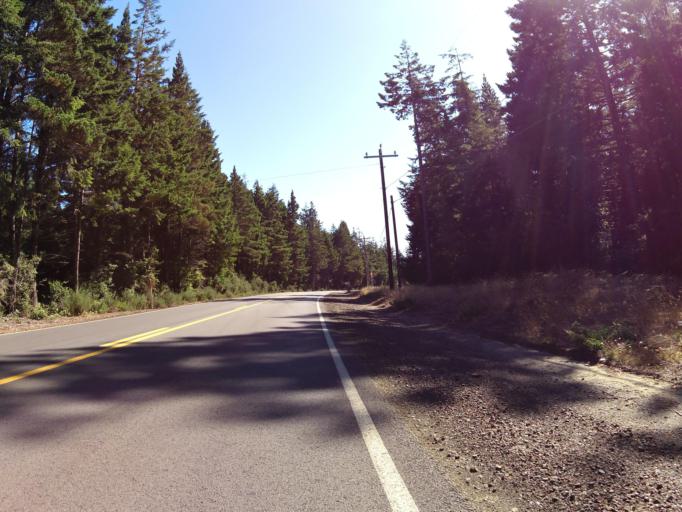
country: US
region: Oregon
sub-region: Coos County
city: Bandon
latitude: 43.2037
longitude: -124.3665
